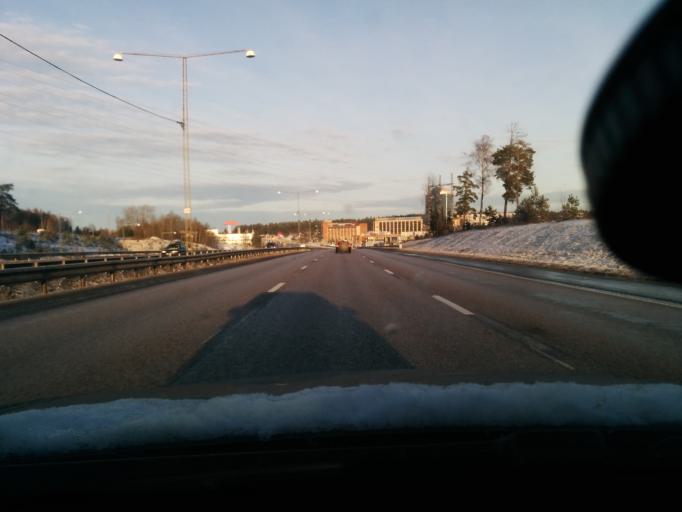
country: SE
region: Stockholm
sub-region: Upplands Vasby Kommun
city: Upplands Vaesby
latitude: 59.4934
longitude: 17.9211
